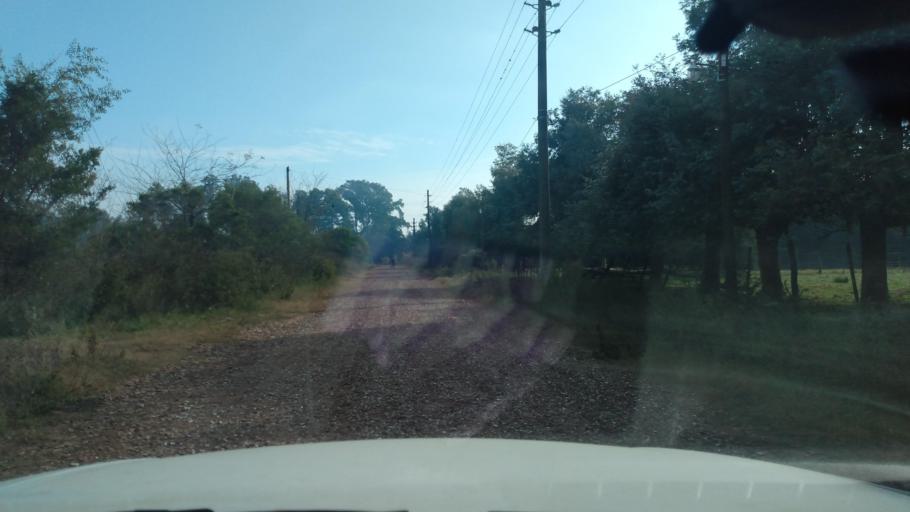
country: AR
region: Buenos Aires
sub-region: Partido de Lujan
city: Lujan
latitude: -34.5875
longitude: -59.1273
